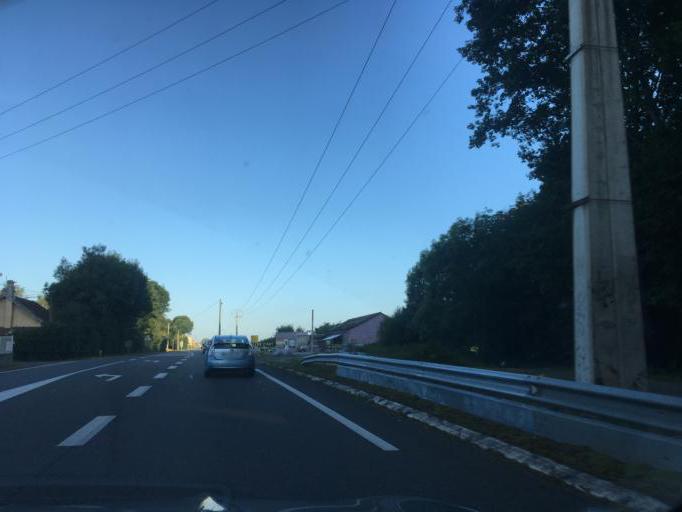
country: FR
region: Midi-Pyrenees
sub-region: Departement des Hautes-Pyrenees
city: Ibos
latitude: 43.2447
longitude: -0.0228
